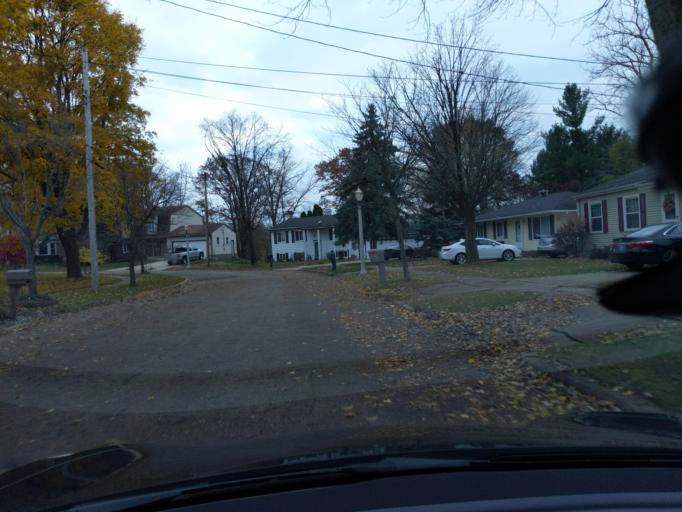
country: US
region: Michigan
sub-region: Ingham County
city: Lansing
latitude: 42.7557
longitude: -84.5632
